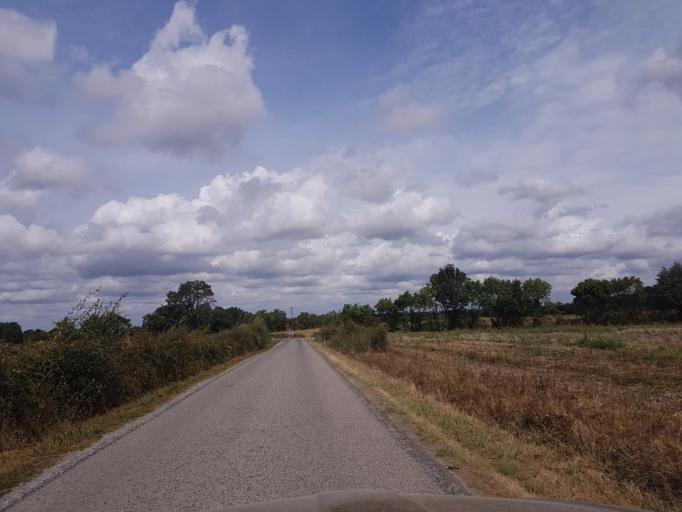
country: FR
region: Pays de la Loire
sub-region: Departement de la Loire-Atlantique
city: Petit-Mars
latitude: 47.4090
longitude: -1.4310
